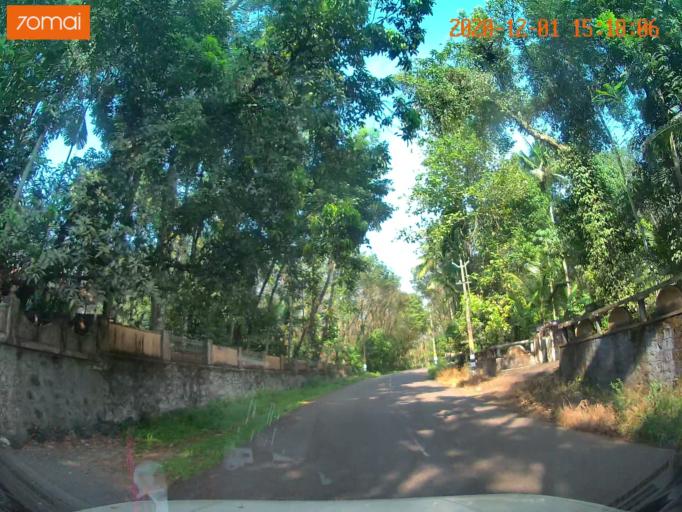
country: IN
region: Kerala
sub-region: Ernakulam
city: Ramamangalam
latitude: 9.9347
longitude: 76.5295
